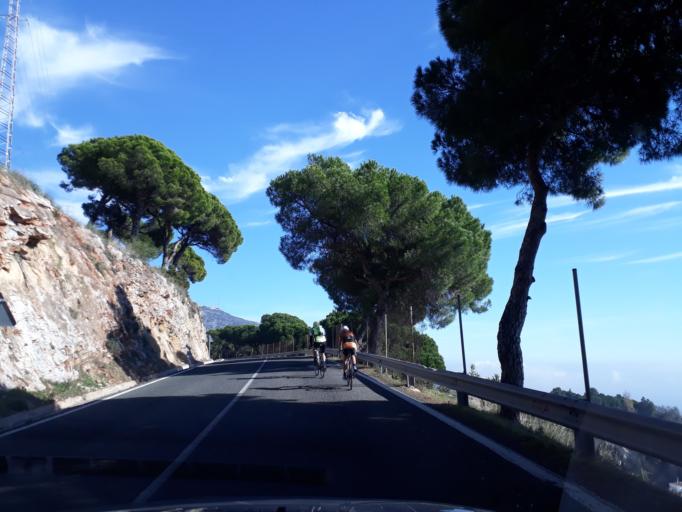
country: ES
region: Andalusia
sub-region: Provincia de Malaga
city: Mijas
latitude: 36.5945
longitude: -4.6437
